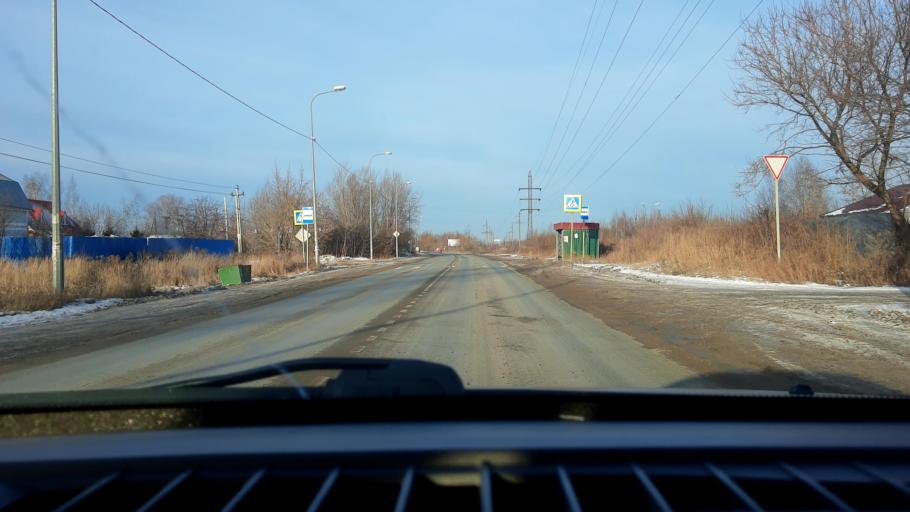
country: RU
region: Nizjnij Novgorod
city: Bor
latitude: 56.3730
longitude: 44.0636
